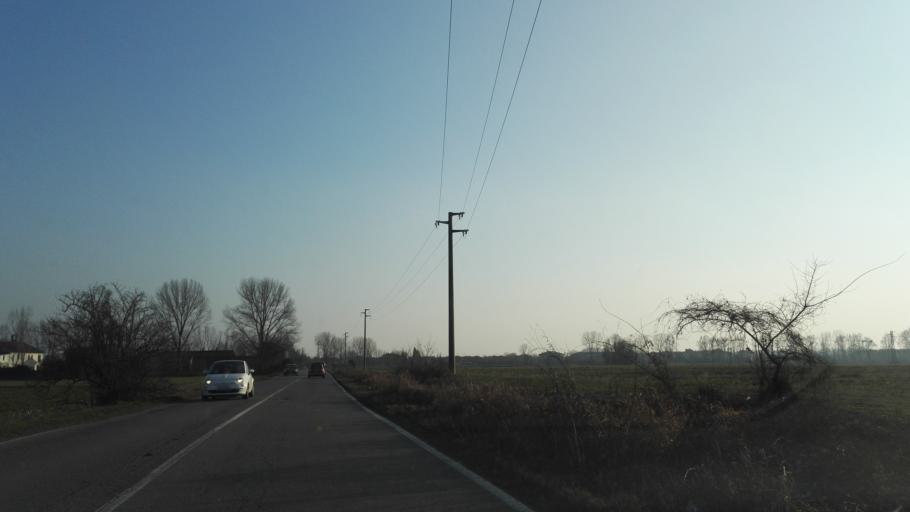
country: IT
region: Lombardy
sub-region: Citta metropolitana di Milano
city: Caleppio
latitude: 45.4252
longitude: 9.3776
